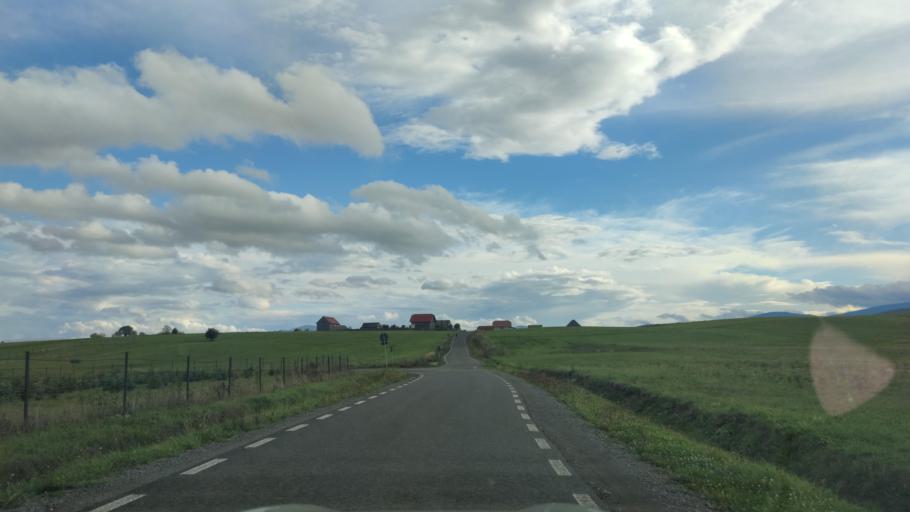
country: RO
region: Harghita
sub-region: Comuna Remetea
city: Remetea
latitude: 46.8049
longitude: 25.4317
